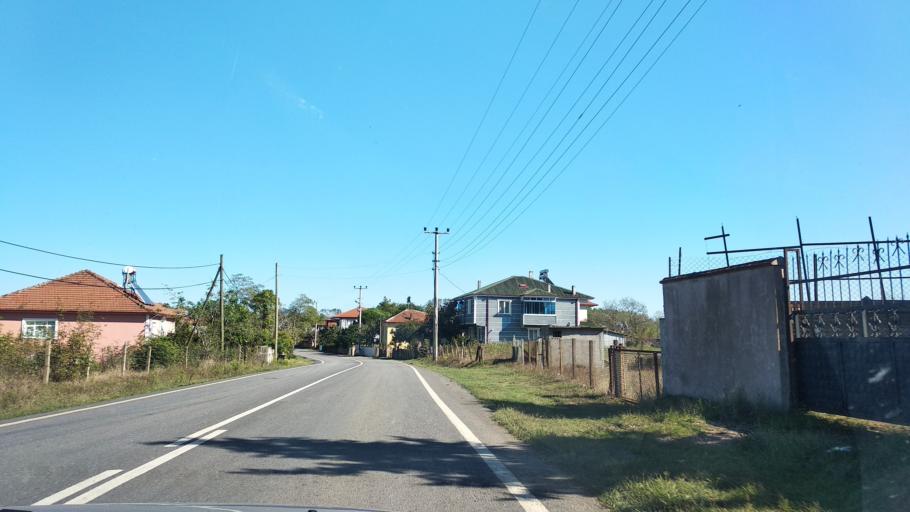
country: TR
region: Sakarya
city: Karasu
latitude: 41.1181
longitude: 30.6202
